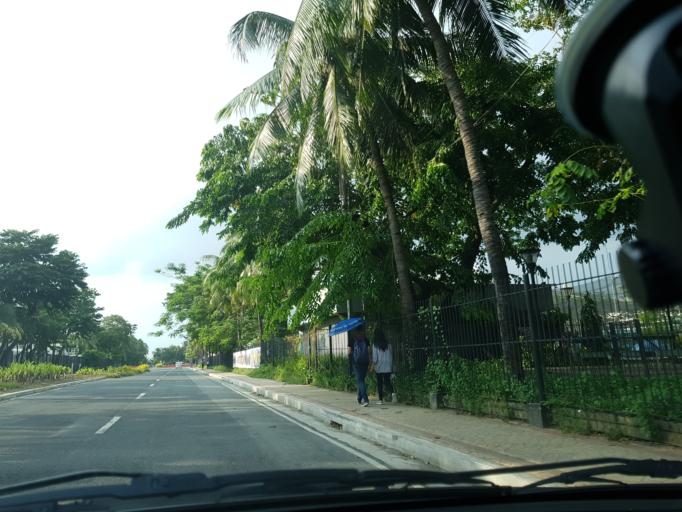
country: PH
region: Metro Manila
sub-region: City of Manila
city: Port Area
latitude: 14.5549
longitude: 120.9850
